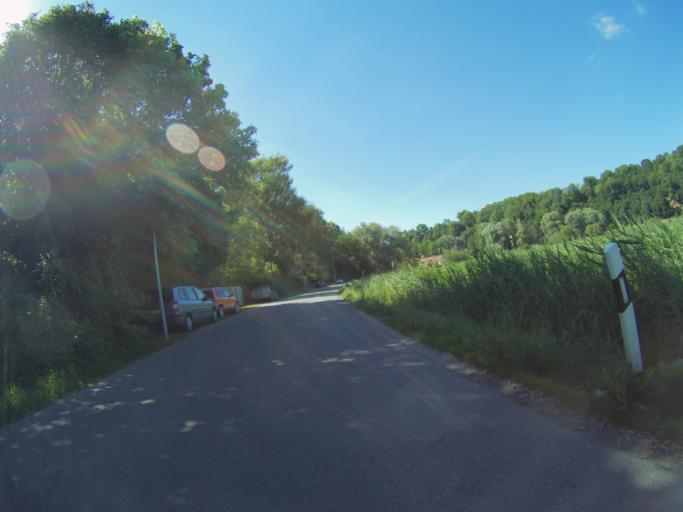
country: DE
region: Bavaria
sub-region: Upper Bavaria
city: Freising
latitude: 48.3914
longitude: 11.7257
